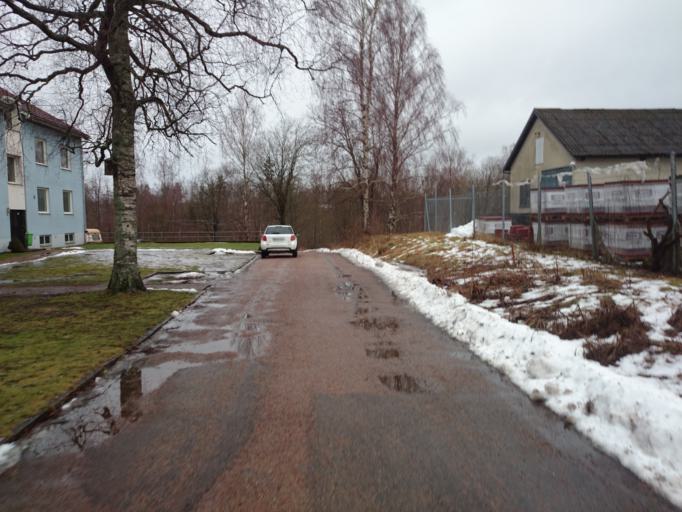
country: SE
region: Halland
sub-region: Hylte Kommun
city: Hyltebruk
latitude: 57.0014
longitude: 13.2514
